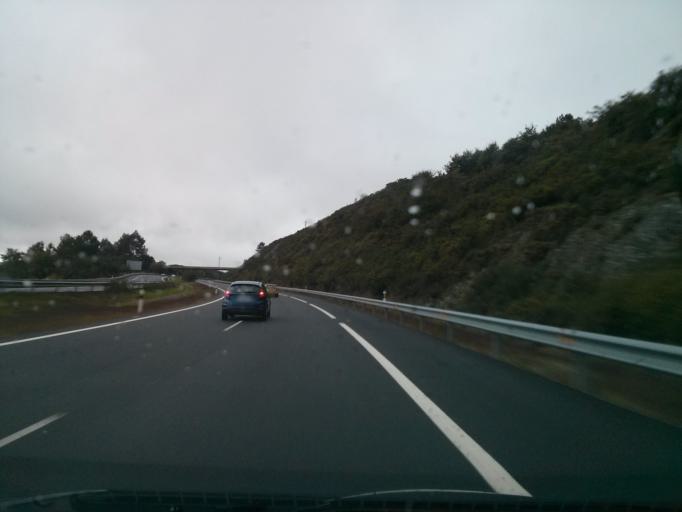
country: ES
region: Galicia
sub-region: Provincia de Ourense
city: Melon
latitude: 42.2267
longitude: -8.2401
